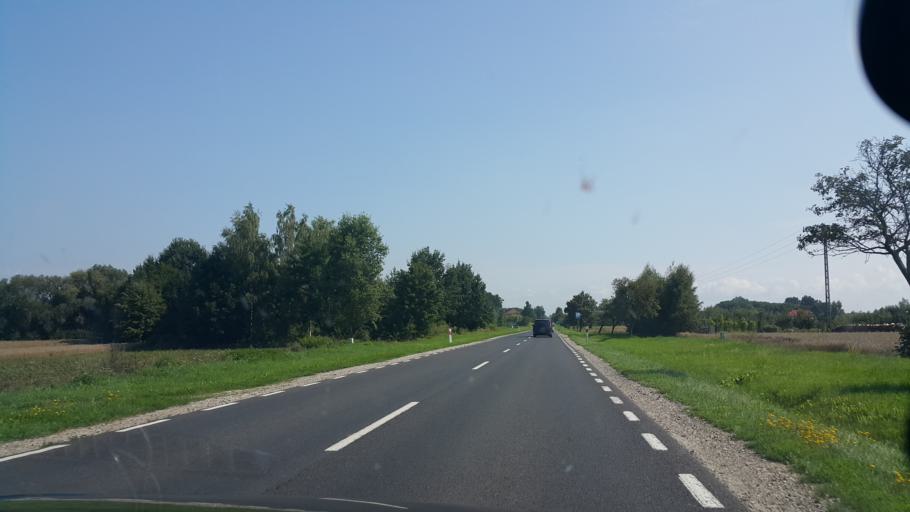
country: PL
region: Lublin Voivodeship
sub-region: Powiat leczynski
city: Cycow
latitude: 51.2973
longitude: 23.1145
